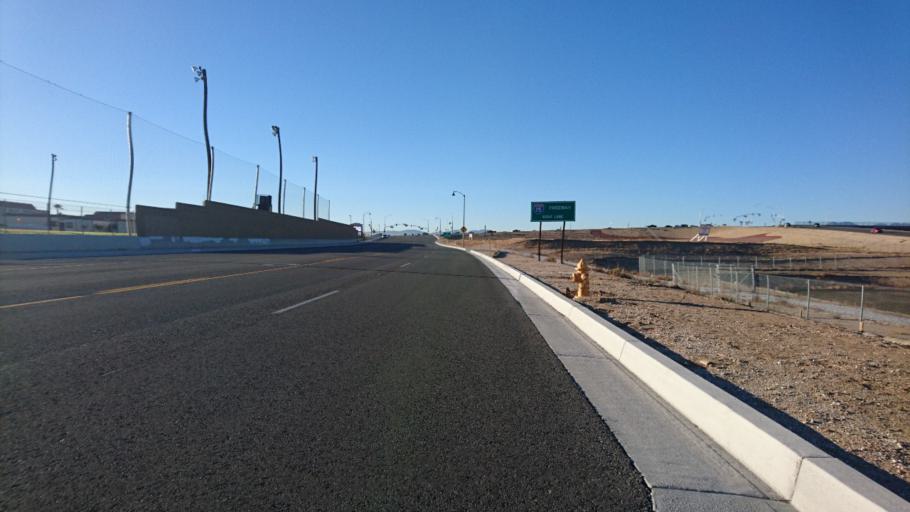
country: US
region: California
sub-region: San Bernardino County
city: Mountain View Acres
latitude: 34.4884
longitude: -117.3323
